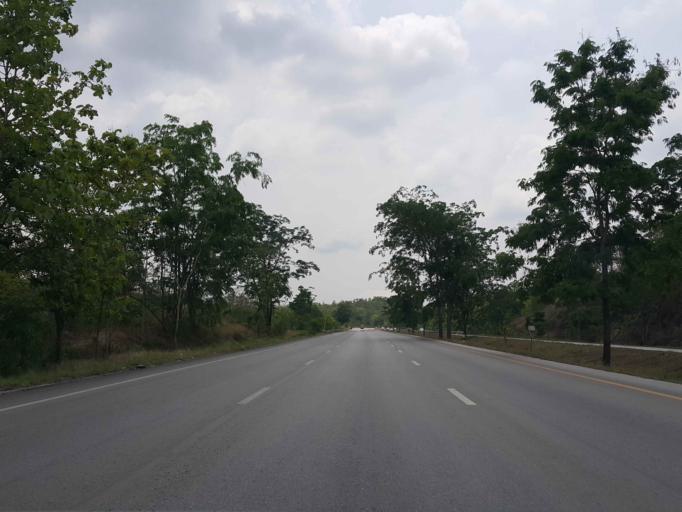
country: TH
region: Lampang
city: Soem Ngam
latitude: 18.0500
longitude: 99.3853
